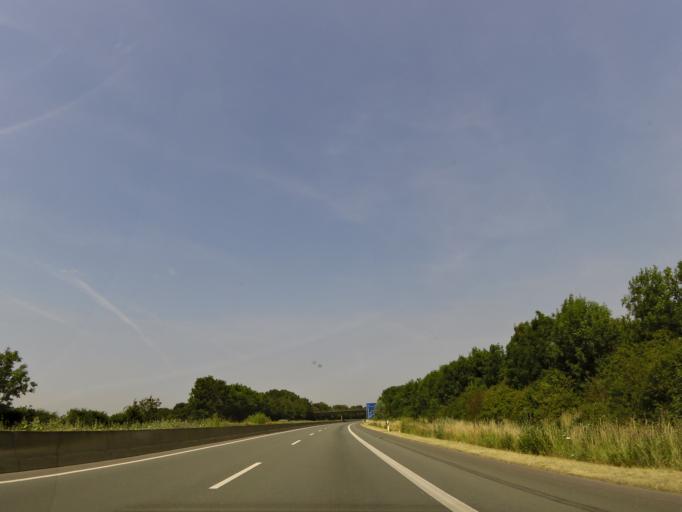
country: DE
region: North Rhine-Westphalia
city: Tuernich
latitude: 50.8498
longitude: 6.7333
